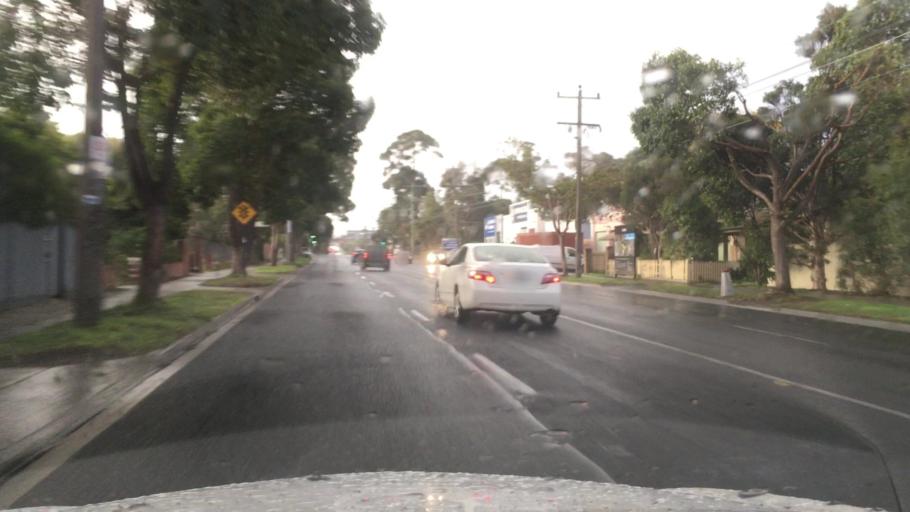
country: AU
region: Victoria
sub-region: Whitehorse
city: Box Hill South
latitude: -37.8271
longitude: 145.1221
